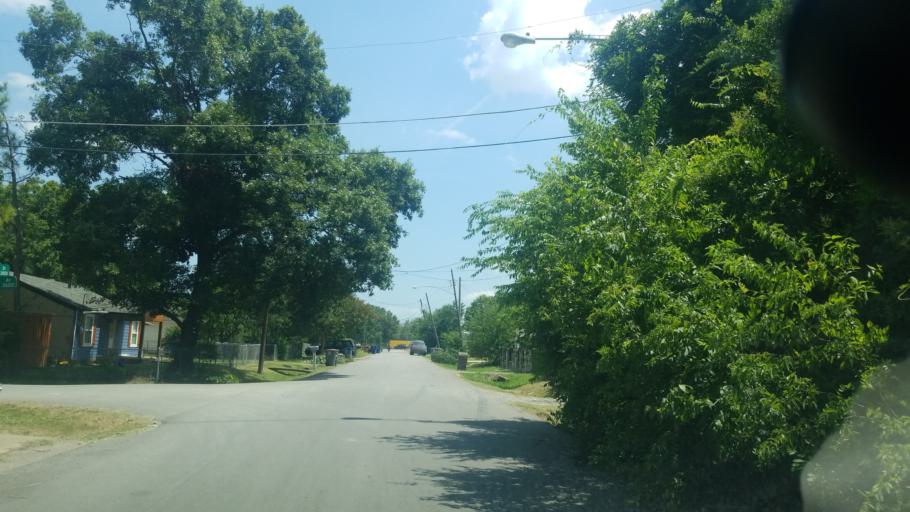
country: US
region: Texas
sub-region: Dallas County
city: Dallas
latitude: 32.7173
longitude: -96.7658
